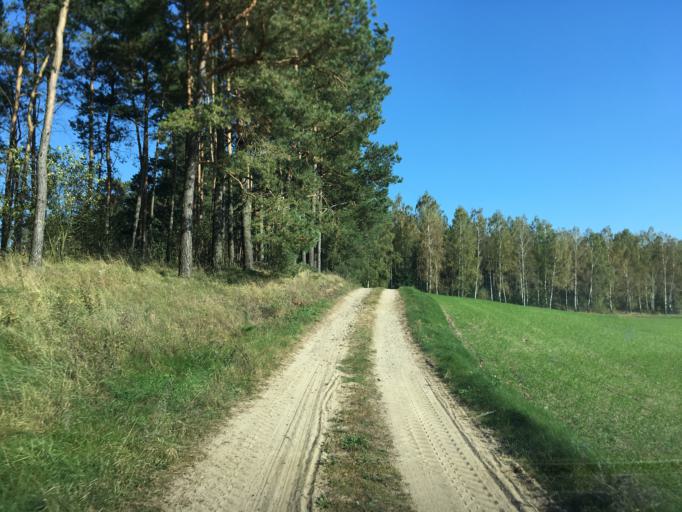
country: PL
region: Warmian-Masurian Voivodeship
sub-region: Powiat dzialdowski
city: Rybno
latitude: 53.4068
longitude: 19.9035
